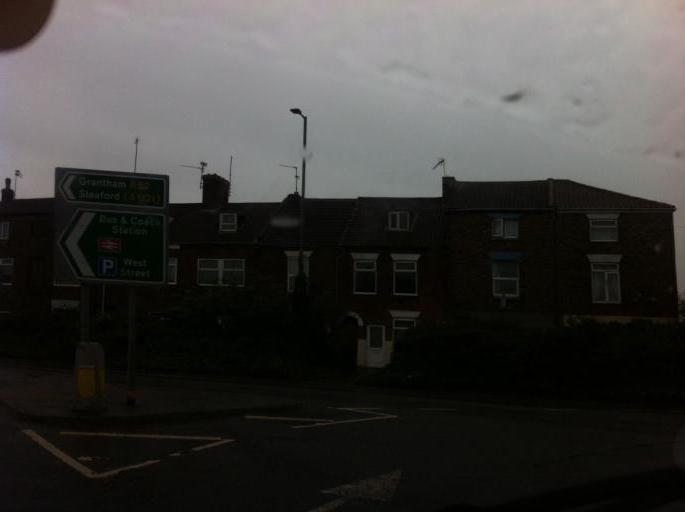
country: GB
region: England
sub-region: Lincolnshire
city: Boston
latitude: 52.9740
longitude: -0.0279
